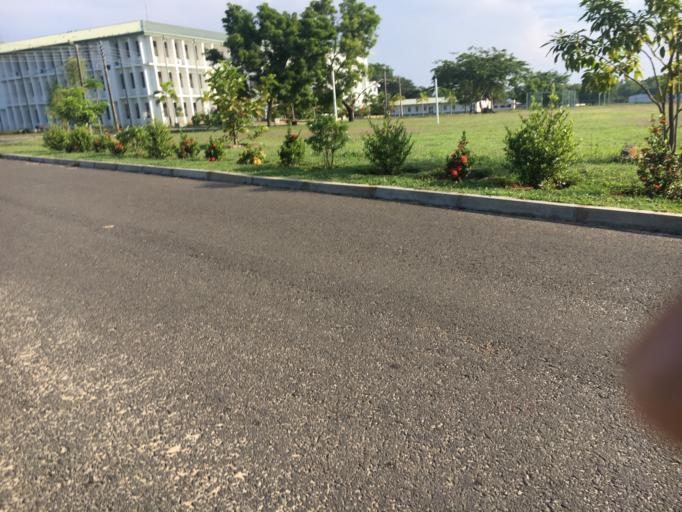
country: LK
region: Eastern Province
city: Eravur Town
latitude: 7.7960
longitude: 81.5795
